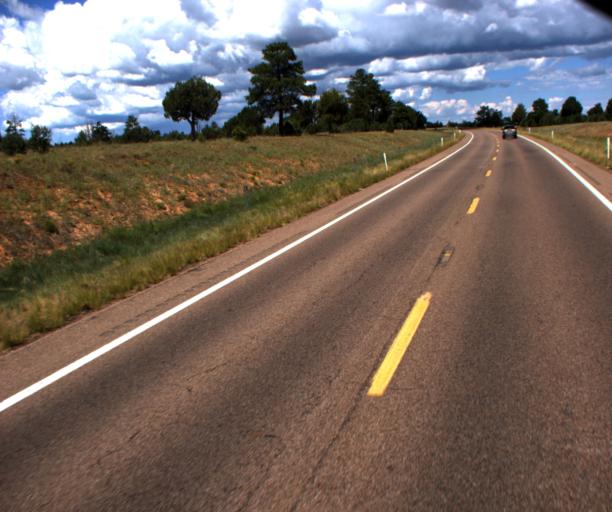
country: US
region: Arizona
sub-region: Navajo County
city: Heber-Overgaard
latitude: 34.3780
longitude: -110.4676
